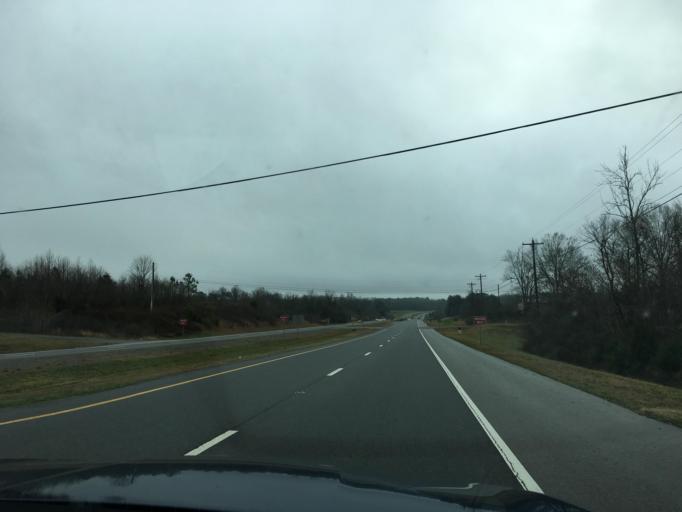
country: US
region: Tennessee
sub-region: McMinn County
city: Athens
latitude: 35.3919
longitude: -84.5676
